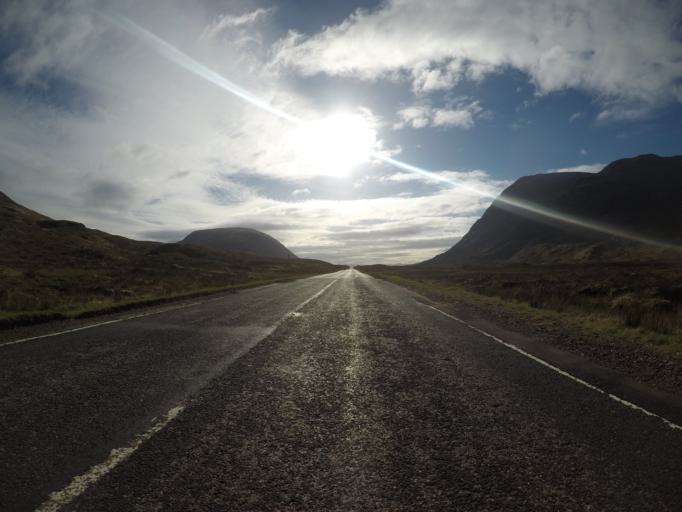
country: GB
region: Scotland
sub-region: Highland
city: Spean Bridge
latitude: 56.6627
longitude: -4.9280
